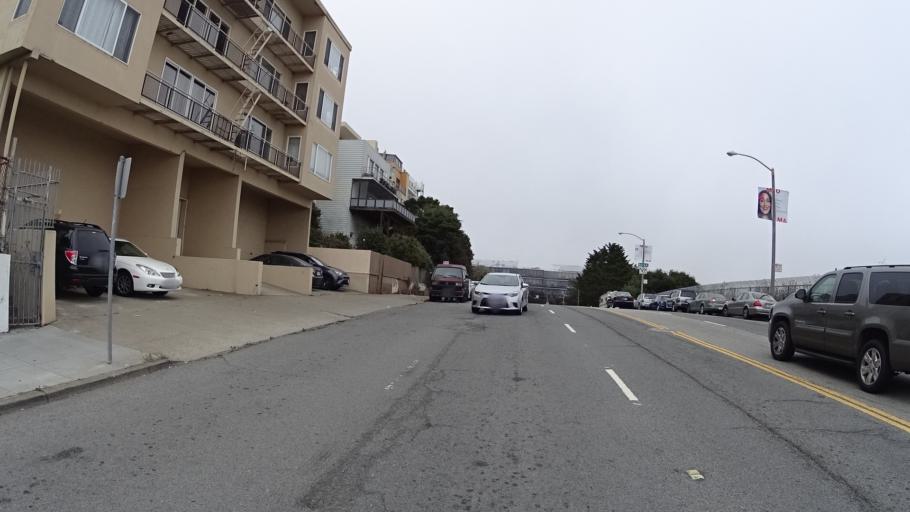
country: US
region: California
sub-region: San Francisco County
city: San Francisco
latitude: 37.7837
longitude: -122.4473
